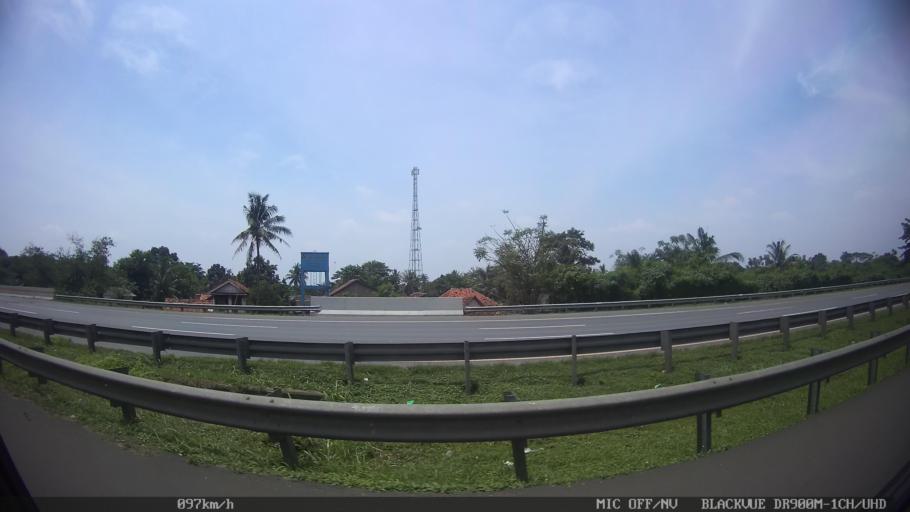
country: ID
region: West Java
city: Kresek
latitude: -6.1806
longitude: 106.3919
